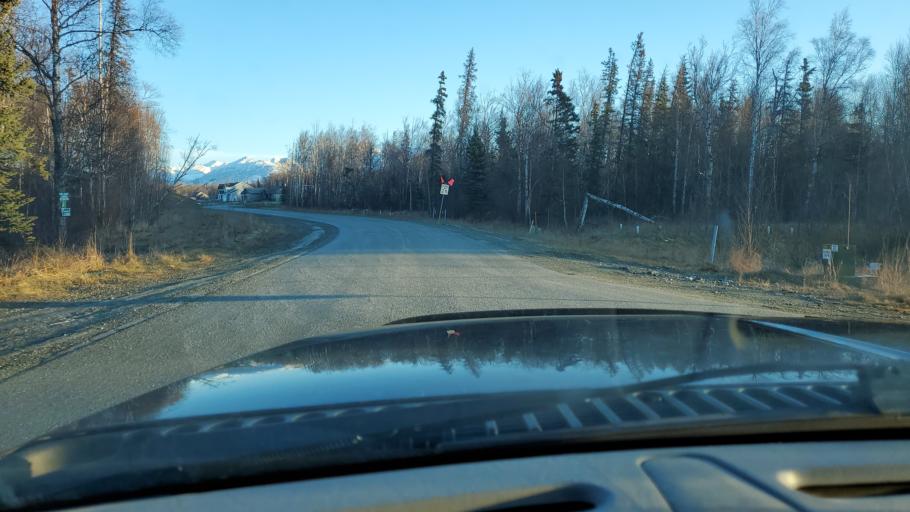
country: US
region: Alaska
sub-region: Matanuska-Susitna Borough
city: Gateway
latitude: 61.5857
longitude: -149.2650
